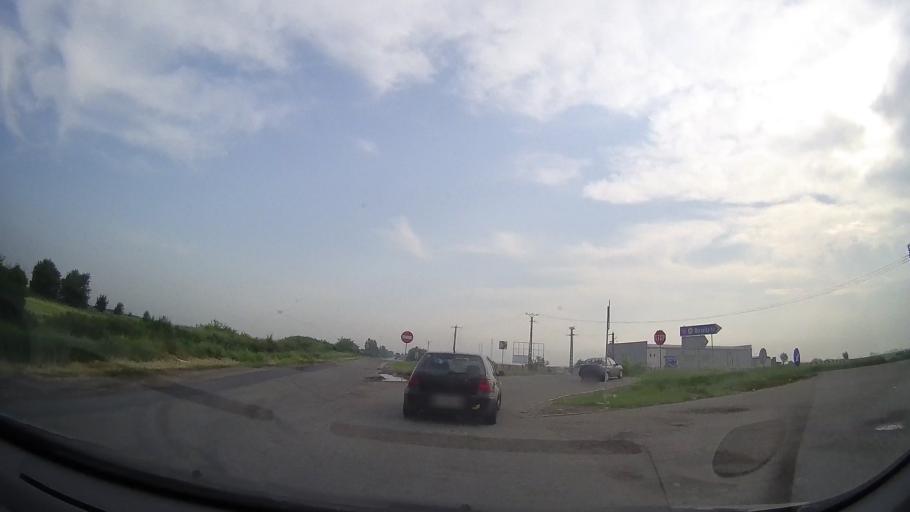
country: RO
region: Timis
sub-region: Comuna Sag
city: Sag
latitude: 45.6836
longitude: 21.1683
